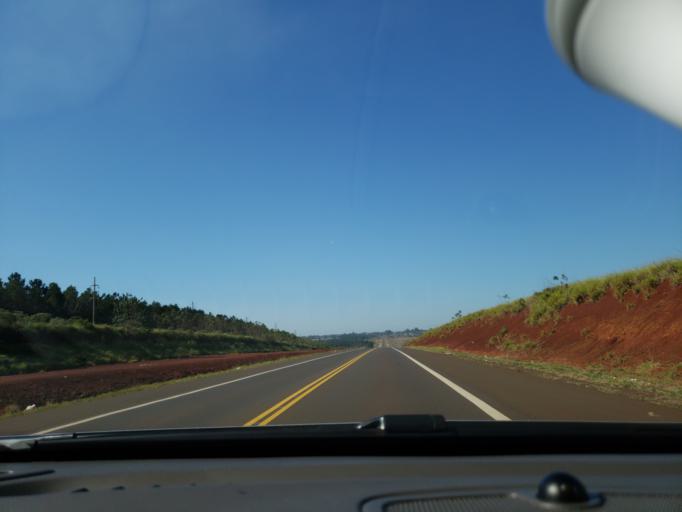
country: AR
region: Misiones
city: Garupa
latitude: -27.4654
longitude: -55.9083
